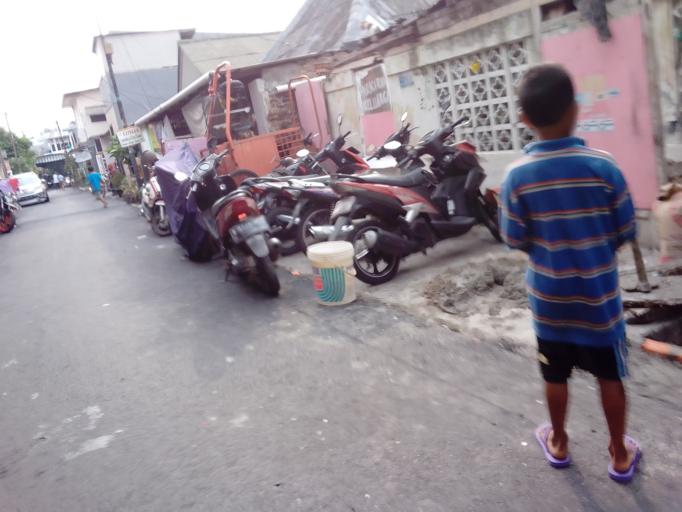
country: ID
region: Jakarta Raya
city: Jakarta
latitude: -6.1790
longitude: 106.8151
